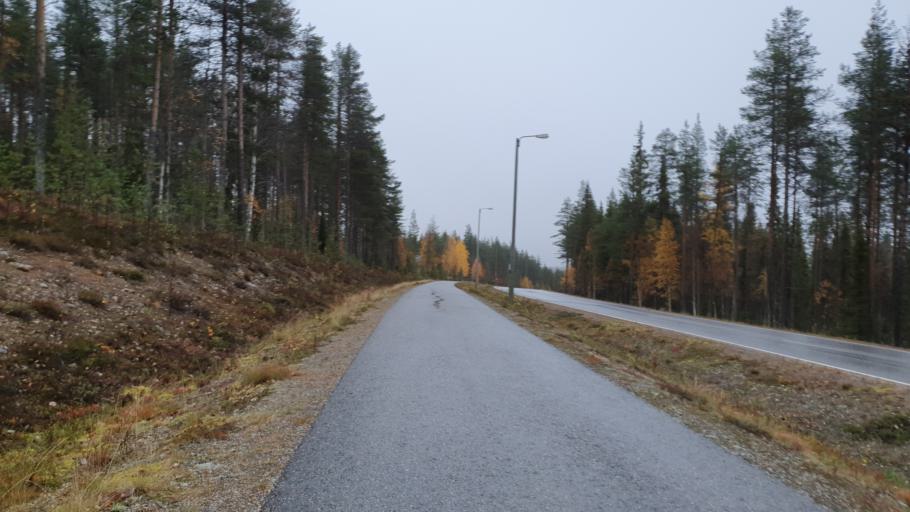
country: FI
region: Lapland
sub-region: Tunturi-Lappi
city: Kolari
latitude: 67.6002
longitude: 24.1244
